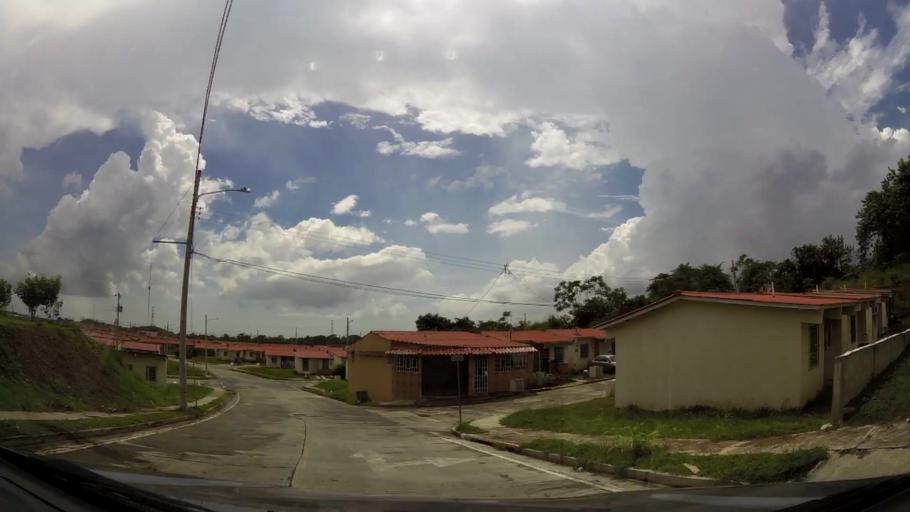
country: PA
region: Panama
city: Cabra Numero Uno
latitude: 9.1232
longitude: -79.3422
